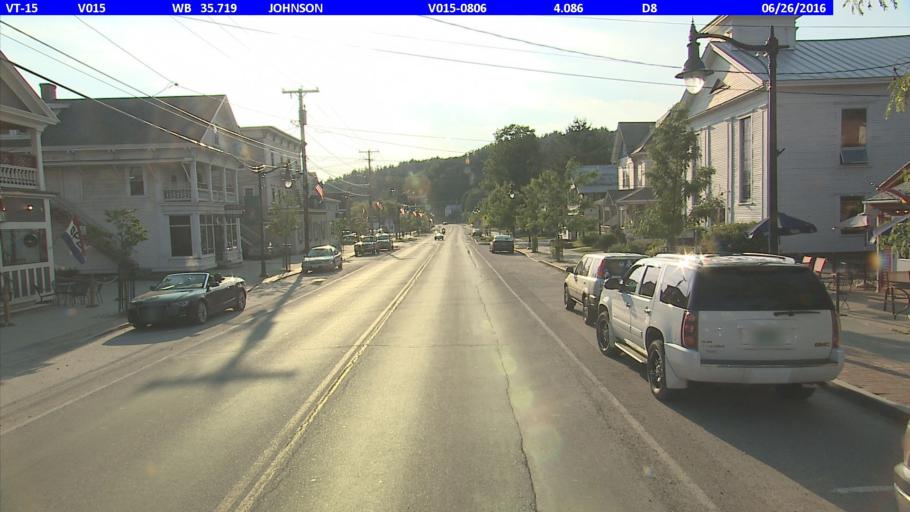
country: US
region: Vermont
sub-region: Lamoille County
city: Johnson
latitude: 44.6353
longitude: -72.6794
